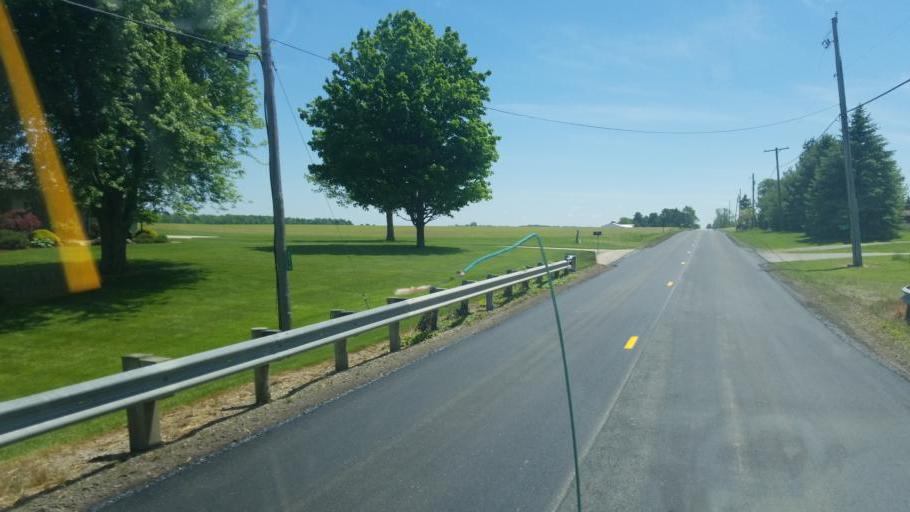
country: US
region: Ohio
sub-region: Huron County
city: Norwalk
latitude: 41.1952
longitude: -82.5899
